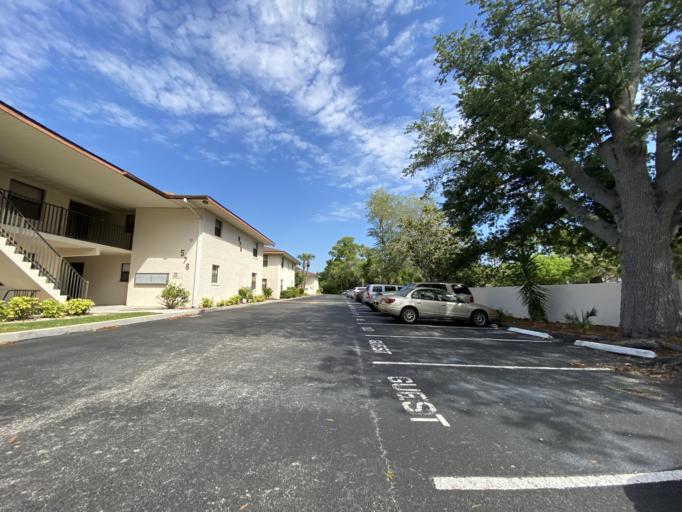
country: US
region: Florida
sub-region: Volusia County
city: South Daytona
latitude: 29.1602
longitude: -81.0011
